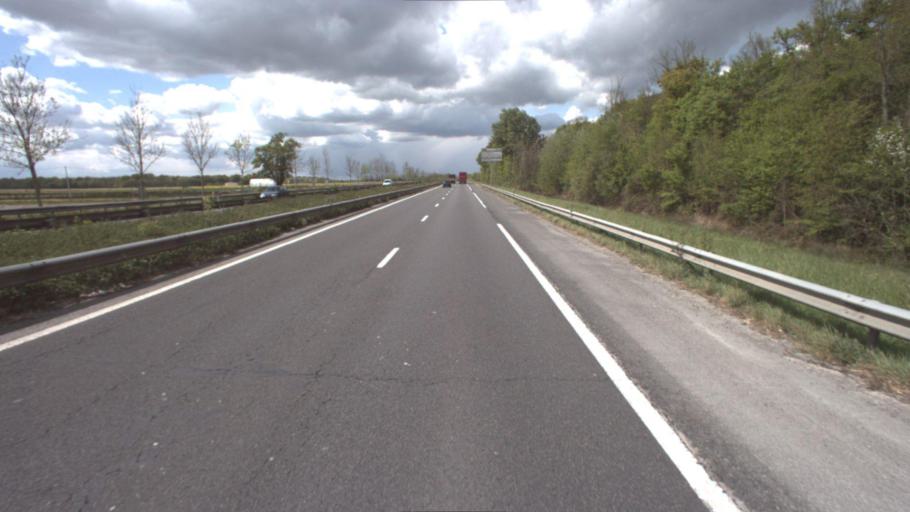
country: FR
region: Ile-de-France
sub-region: Departement de Seine-et-Marne
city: Fontenay-Tresigny
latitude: 48.7237
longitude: 2.8303
